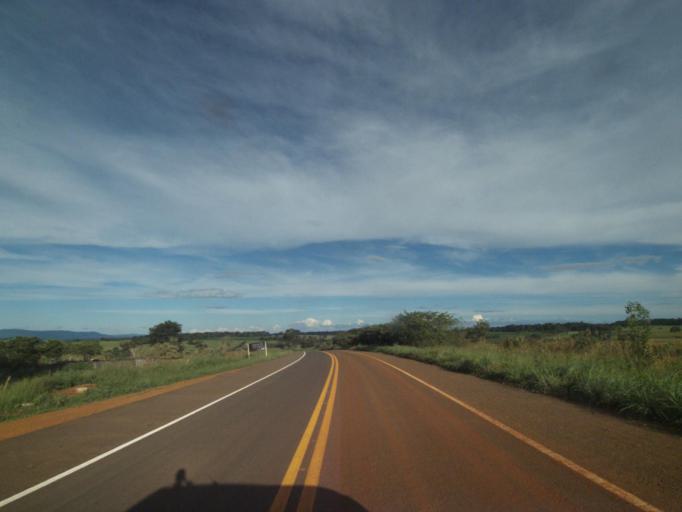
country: BR
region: Goias
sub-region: Jaragua
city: Jaragua
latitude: -15.8954
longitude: -49.5007
